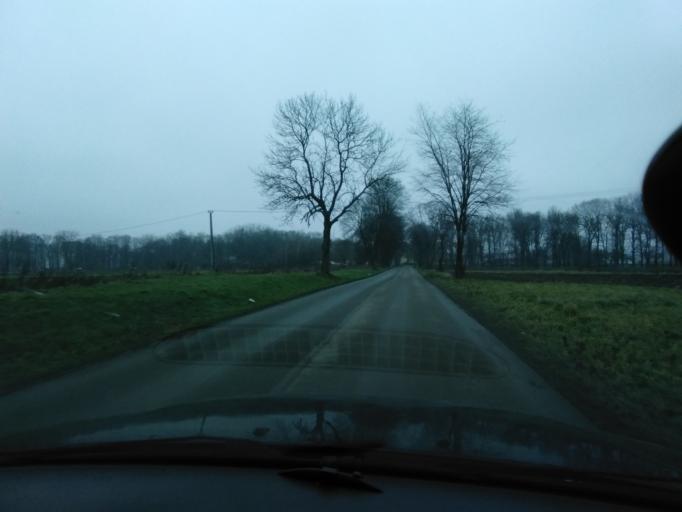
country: PL
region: Subcarpathian Voivodeship
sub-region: Powiat przeworski
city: Zarzecze
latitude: 49.9834
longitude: 22.5485
